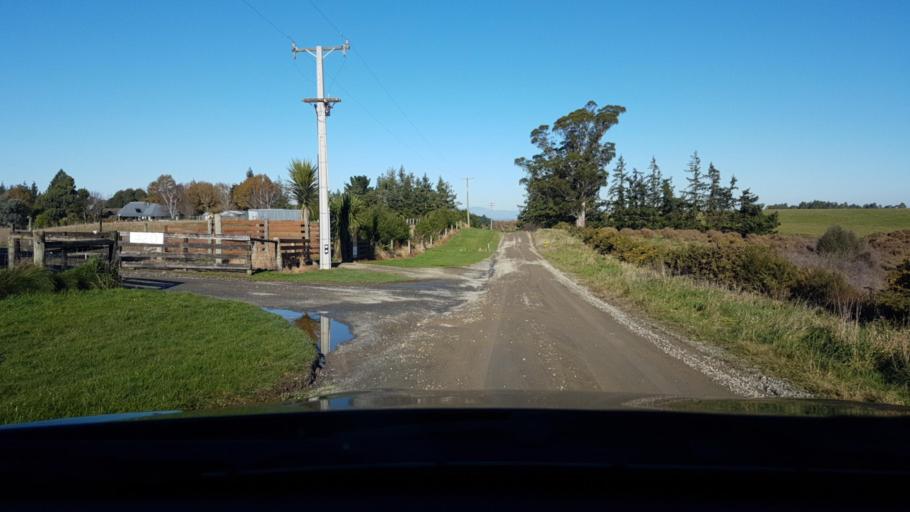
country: NZ
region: Canterbury
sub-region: Waimakariri District
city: Woodend
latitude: -43.2485
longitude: 172.5759
